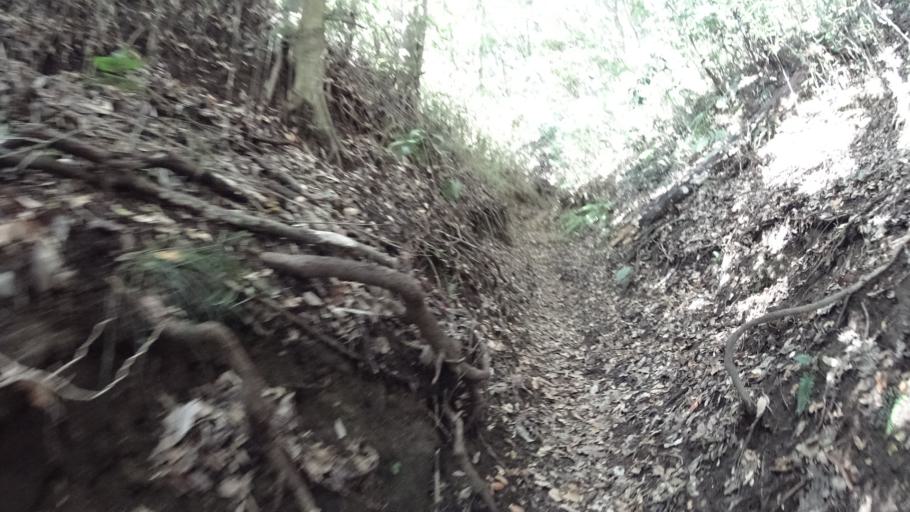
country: JP
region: Kanagawa
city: Kamakura
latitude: 35.3596
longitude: 139.5987
